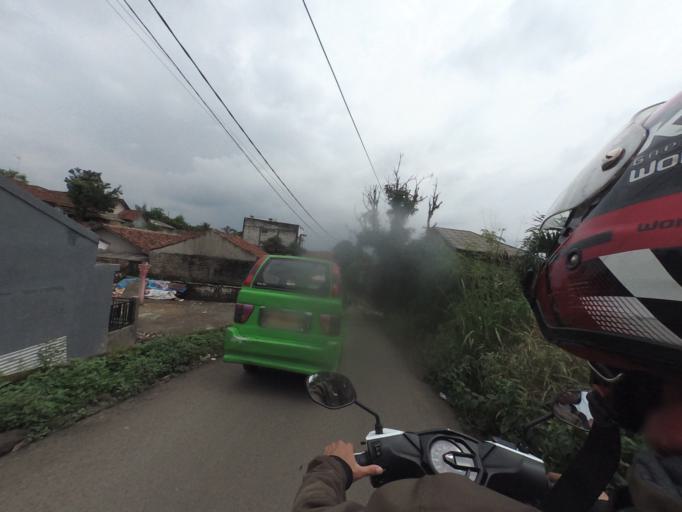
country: ID
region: West Java
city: Bogor
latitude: -6.6077
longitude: 106.7579
